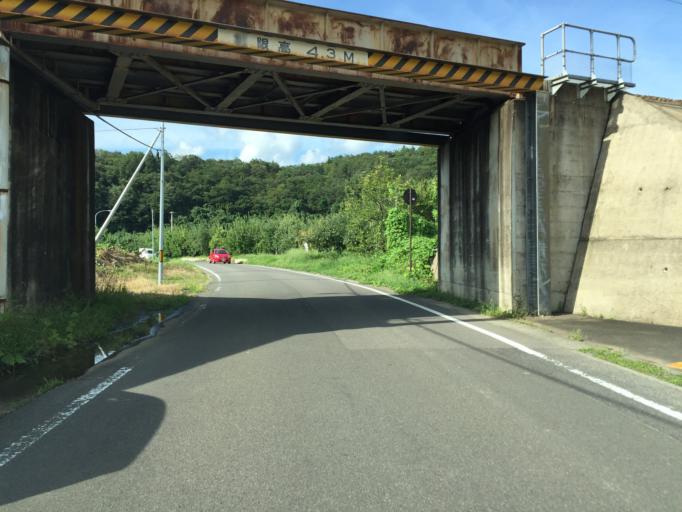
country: JP
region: Fukushima
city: Hobaramachi
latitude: 37.8063
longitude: 140.5097
